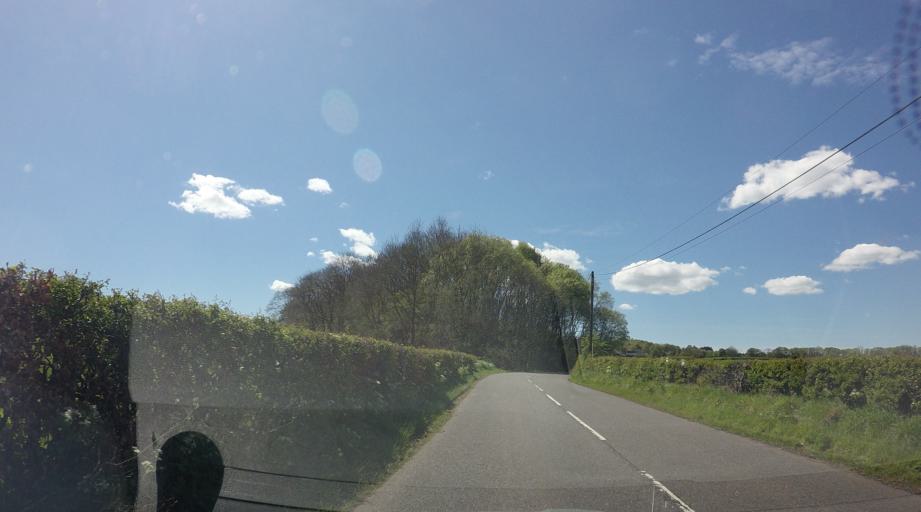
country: GB
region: Scotland
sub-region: West Lothian
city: Linlithgow
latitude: 55.9707
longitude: -3.6554
